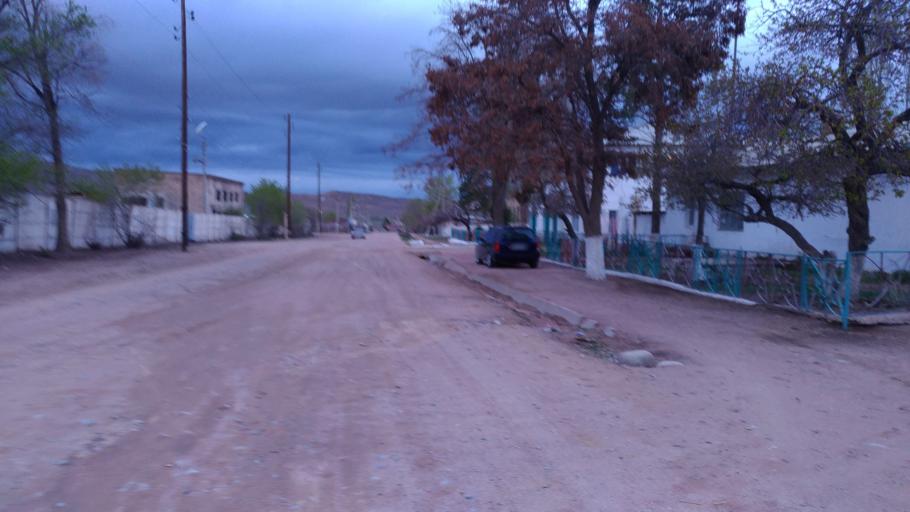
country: KG
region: Ysyk-Koel
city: Bokombayevskoye
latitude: 42.1178
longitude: 76.9881
